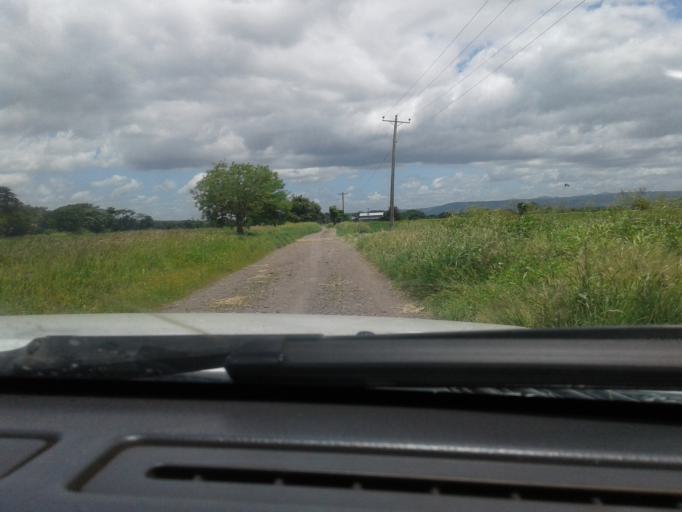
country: NI
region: Matagalpa
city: Ciudad Dario
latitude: 12.8368
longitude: -86.1251
